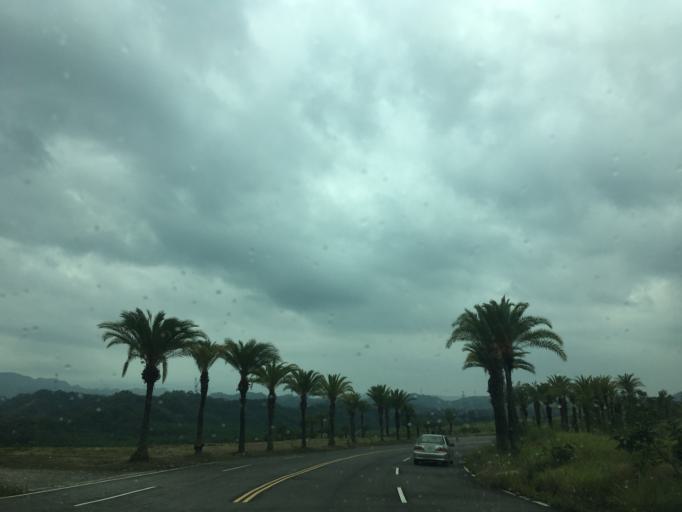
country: TW
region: Taiwan
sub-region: Taichung City
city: Taichung
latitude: 24.0618
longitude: 120.7256
